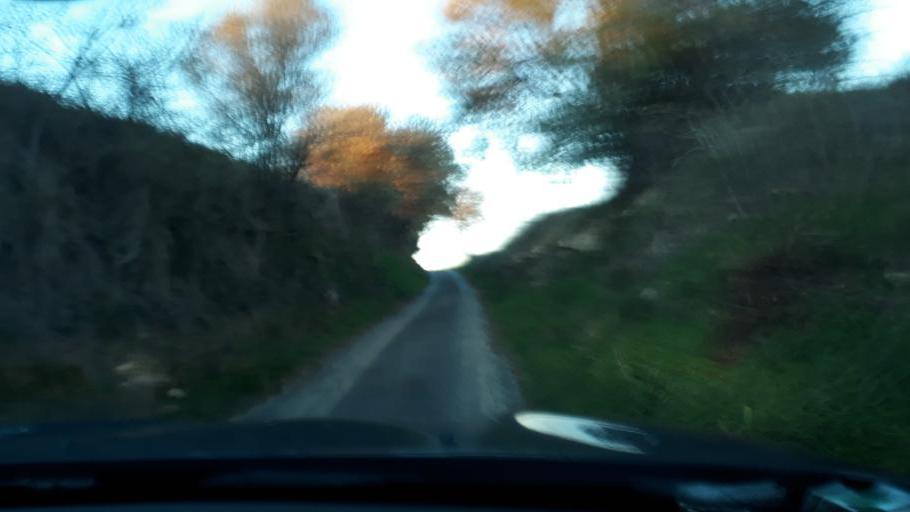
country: FR
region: Languedoc-Roussillon
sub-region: Departement de l'Herault
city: Florensac
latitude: 43.4112
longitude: 3.4588
